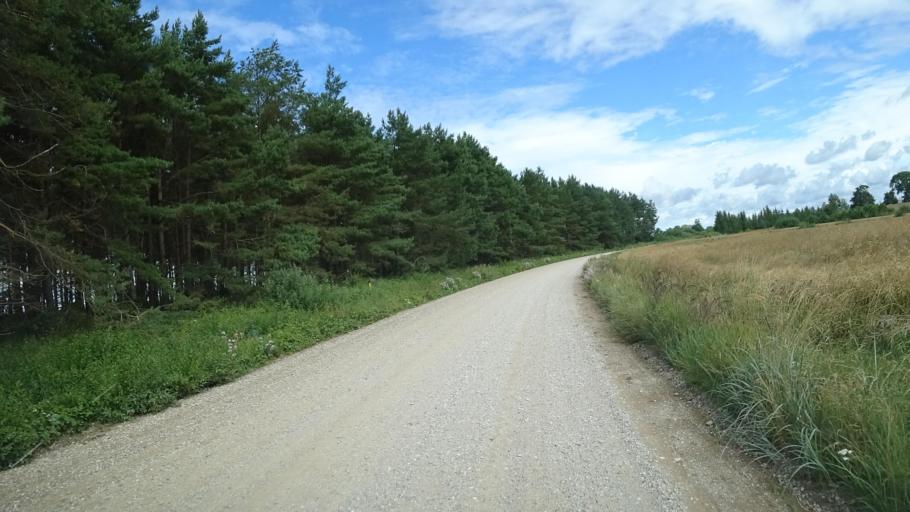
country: LV
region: Liepaja
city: Vec-Liepaja
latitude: 56.6470
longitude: 21.0445
